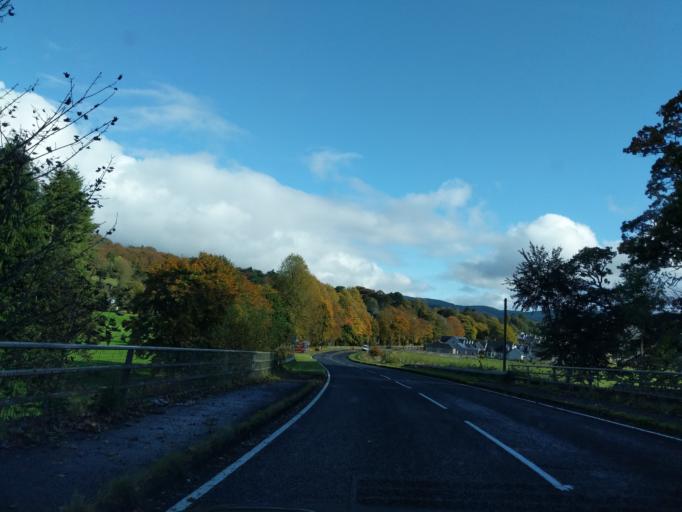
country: GB
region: Scotland
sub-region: Dumfries and Galloway
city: Moffat
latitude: 55.3372
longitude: -3.4533
